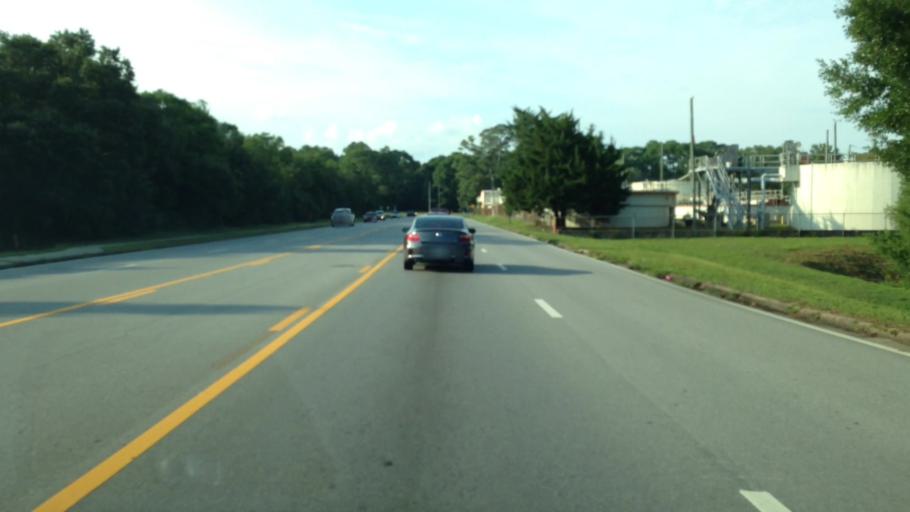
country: US
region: Florida
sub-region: Okaloosa County
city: Mary Esther
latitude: 30.4108
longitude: -86.6647
